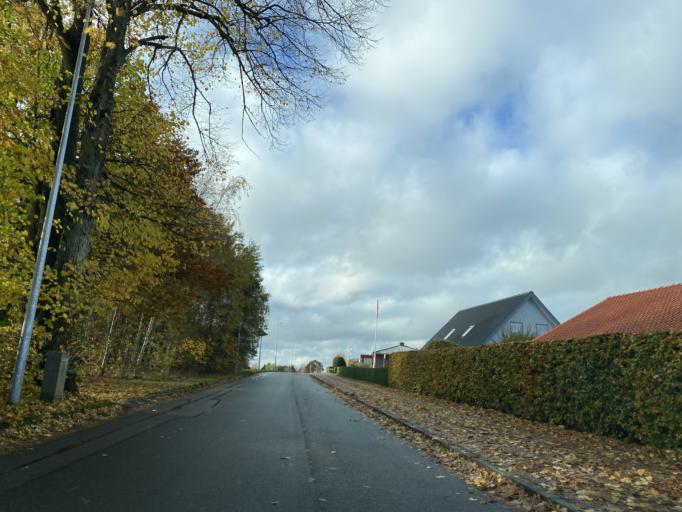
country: DK
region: Central Jutland
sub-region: Favrskov Kommune
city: Hammel
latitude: 56.2552
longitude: 9.8482
